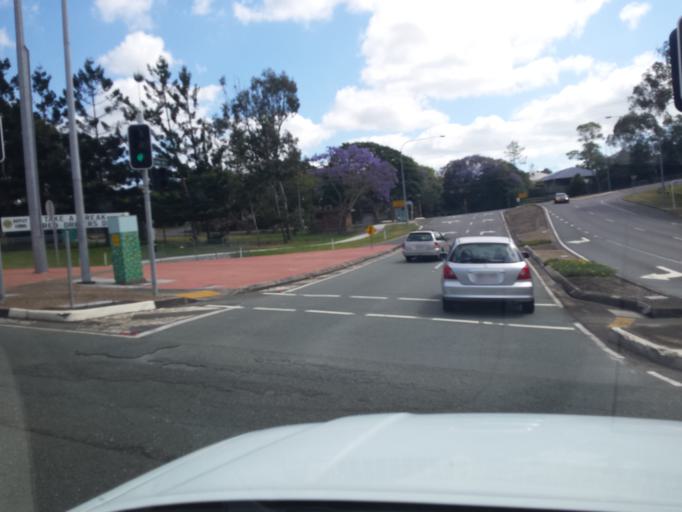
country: AU
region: Queensland
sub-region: Brisbane
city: Chermside West
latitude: -27.3734
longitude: 153.0232
